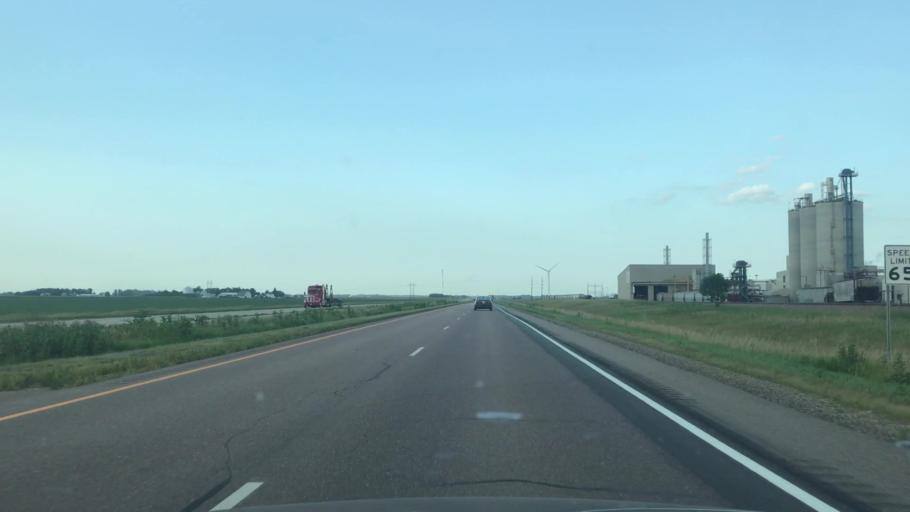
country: US
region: Minnesota
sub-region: Nobles County
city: Worthington
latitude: 43.7046
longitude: -95.4623
